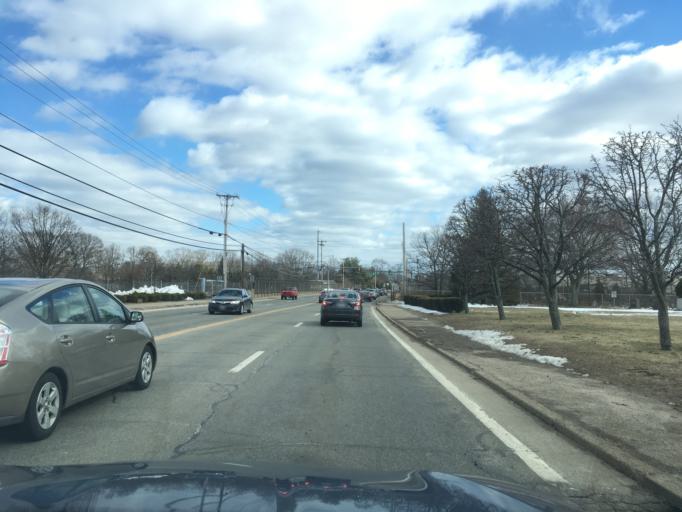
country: US
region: Rhode Island
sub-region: Kent County
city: Warwick
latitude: 41.7229
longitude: -71.4681
